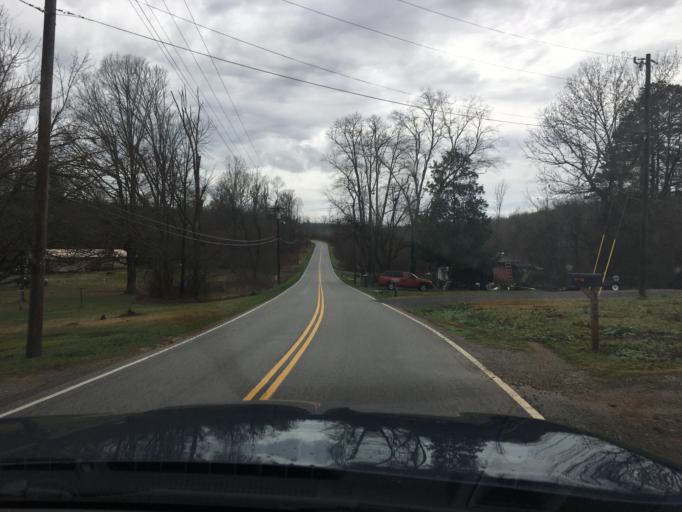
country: US
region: Tennessee
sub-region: Monroe County
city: Madisonville
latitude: 35.3705
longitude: -84.3152
